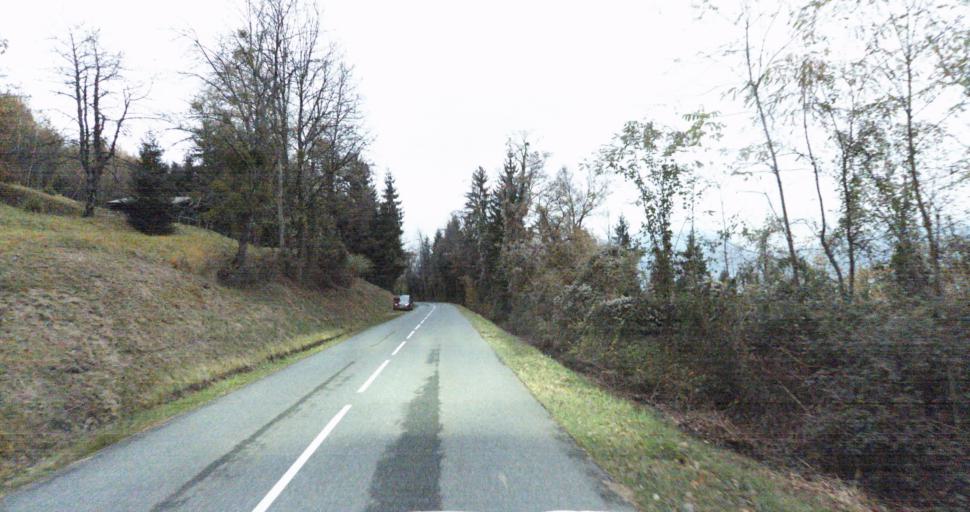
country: FR
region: Rhone-Alpes
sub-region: Departement de la Haute-Savoie
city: Saint-Jorioz
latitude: 45.8338
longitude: 6.1422
